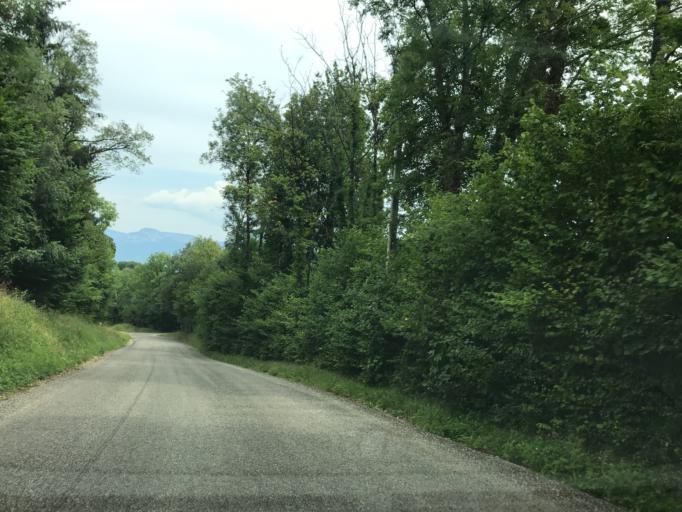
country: FR
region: Rhone-Alpes
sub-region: Departement de l'Isere
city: Chapareillan
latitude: 45.4640
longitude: 5.9665
